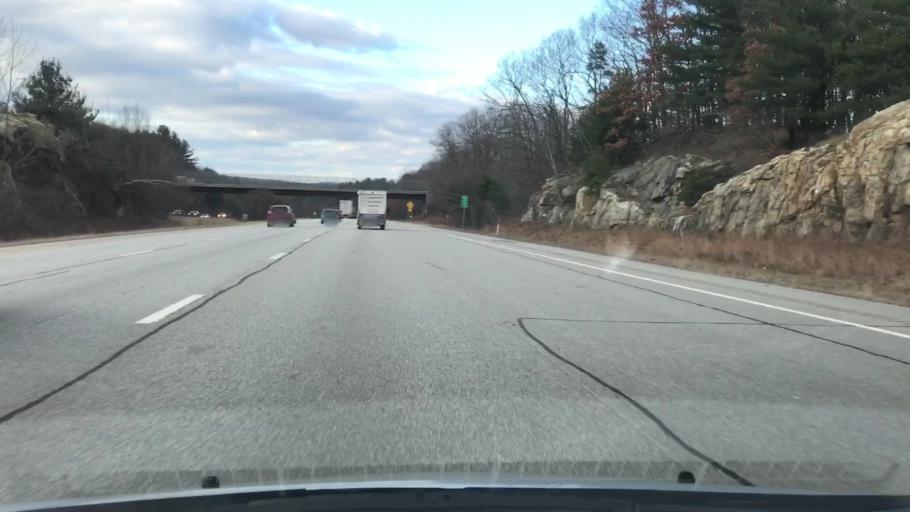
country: US
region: New Hampshire
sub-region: Merrimack County
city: South Hooksett
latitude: 43.0292
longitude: -71.4478
